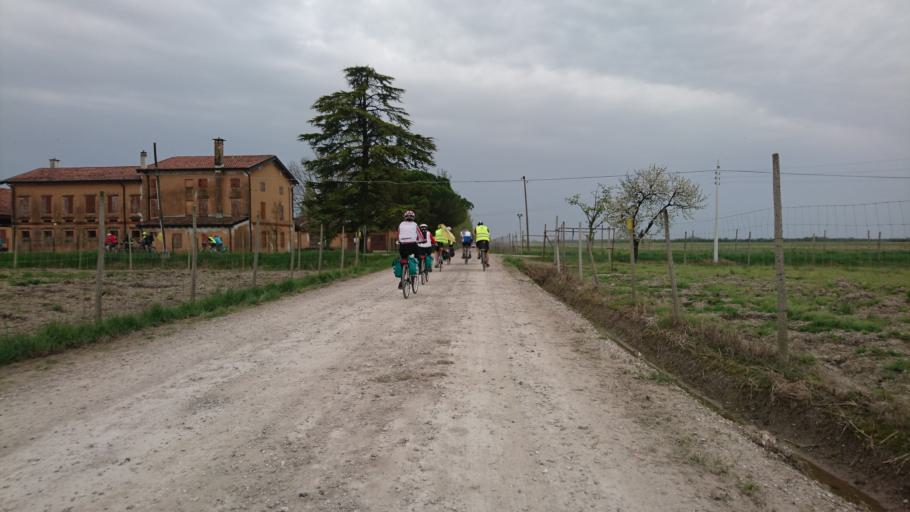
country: IT
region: Veneto
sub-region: Provincia di Venezia
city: Lugugnana
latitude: 45.6877
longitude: 12.9313
